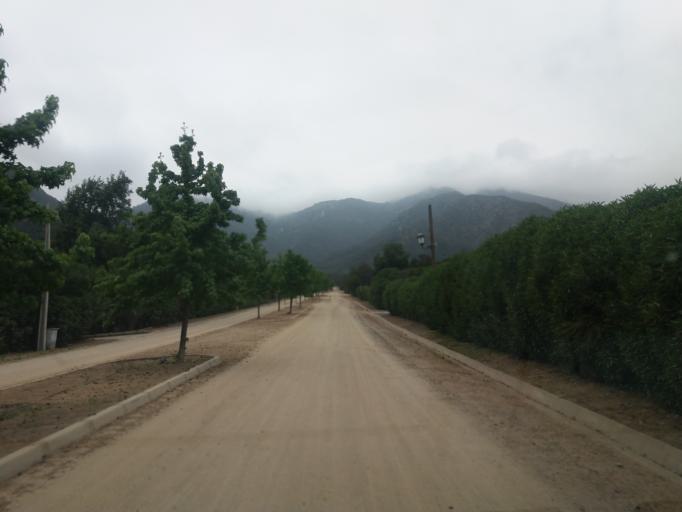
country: CL
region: Valparaiso
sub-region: Provincia de Marga Marga
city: Limache
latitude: -33.0274
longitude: -71.1346
